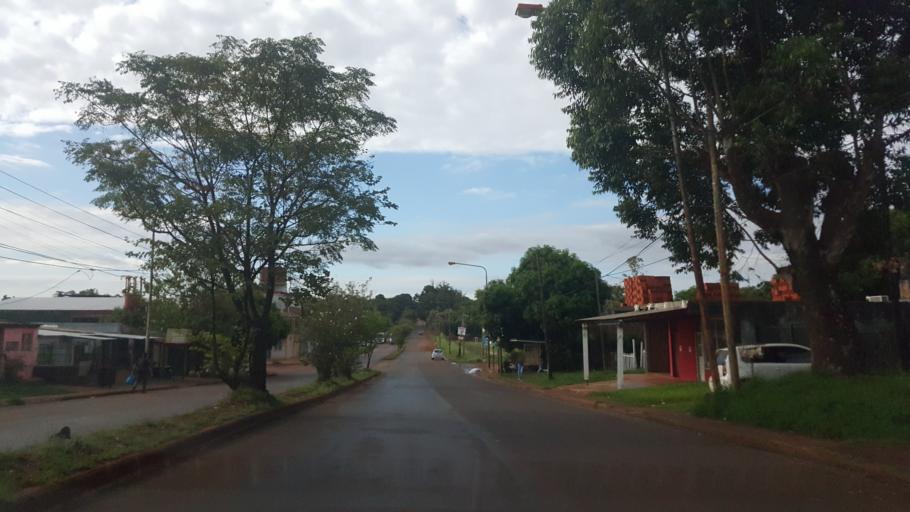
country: AR
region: Misiones
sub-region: Departamento de Capital
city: Posadas
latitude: -27.3948
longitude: -55.9355
